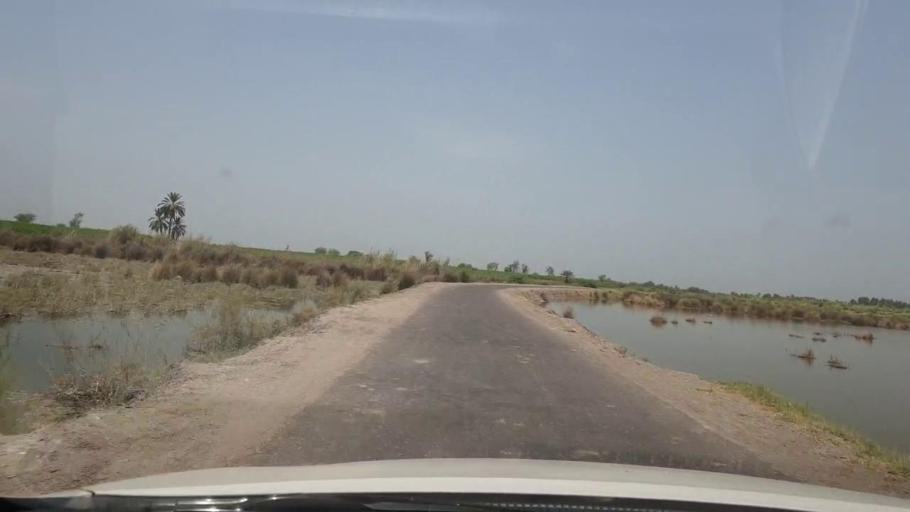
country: PK
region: Sindh
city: Bozdar
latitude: 27.2516
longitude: 68.6417
